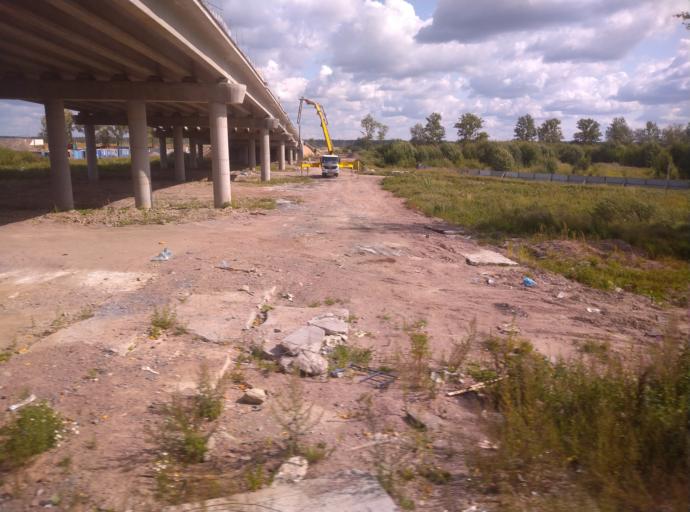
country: RU
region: St.-Petersburg
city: Kolpino
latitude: 59.7333
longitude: 30.6348
